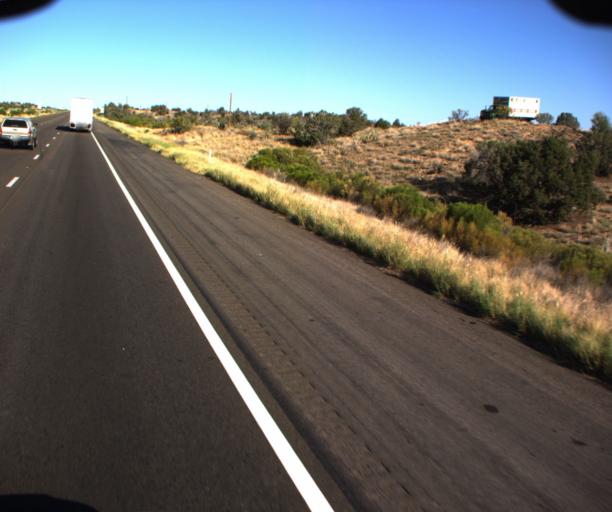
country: US
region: Arizona
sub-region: Mohave County
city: New Kingman-Butler
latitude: 35.1640
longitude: -113.7272
